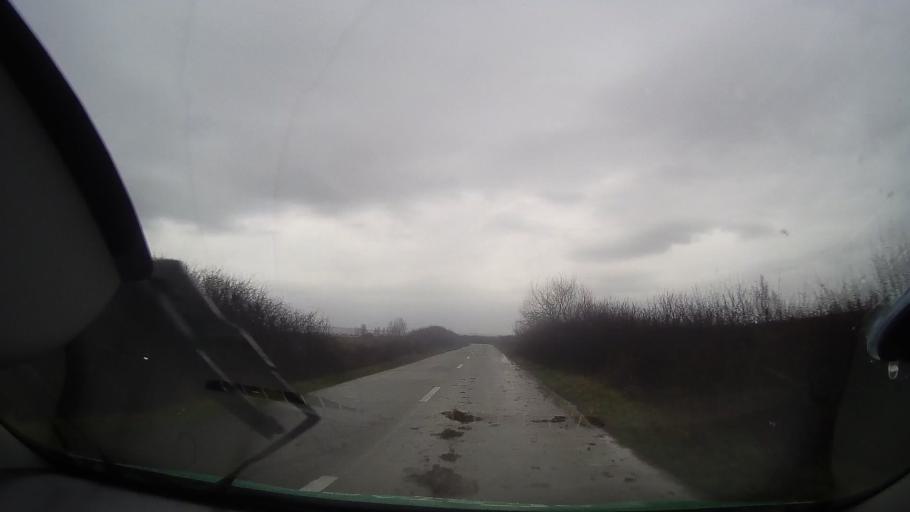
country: RO
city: Capalna
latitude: 46.7267
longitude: 22.0904
